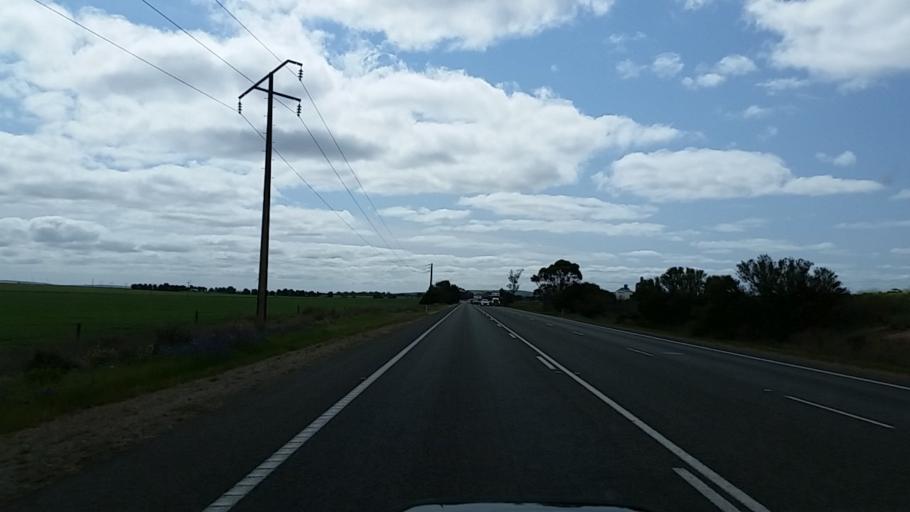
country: AU
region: South Australia
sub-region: Port Pirie City and Dists
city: Crystal Brook
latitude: -33.5564
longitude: 138.2225
